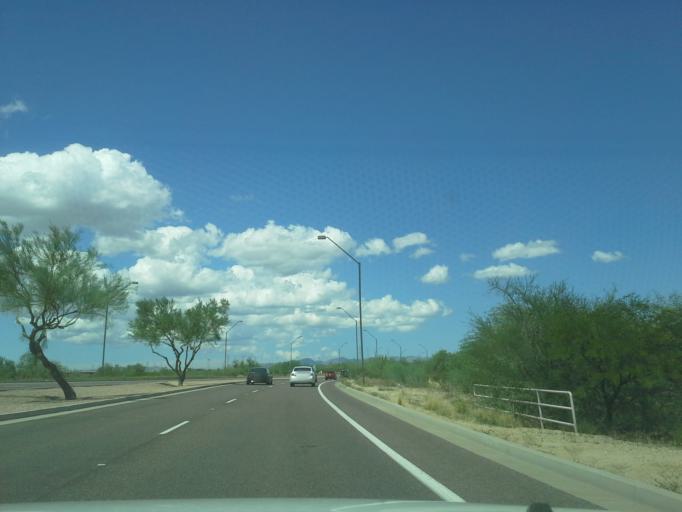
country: US
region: Arizona
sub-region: Maricopa County
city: Paradise Valley
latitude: 33.6573
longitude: -111.9079
